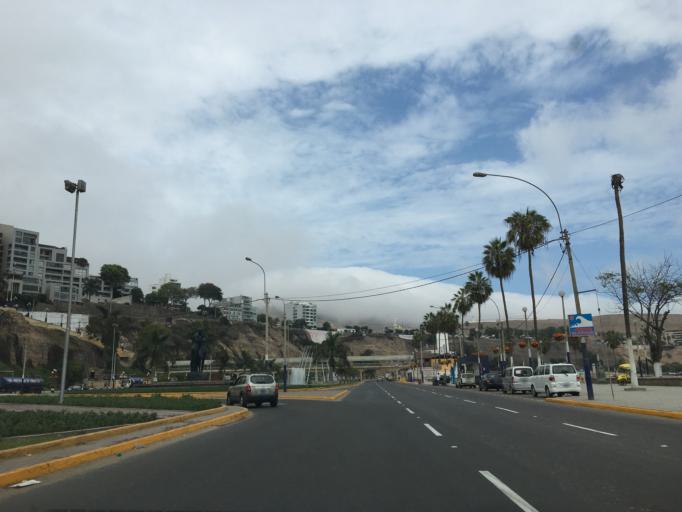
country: PE
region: Lima
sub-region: Lima
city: Surco
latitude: -12.1616
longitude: -77.0258
